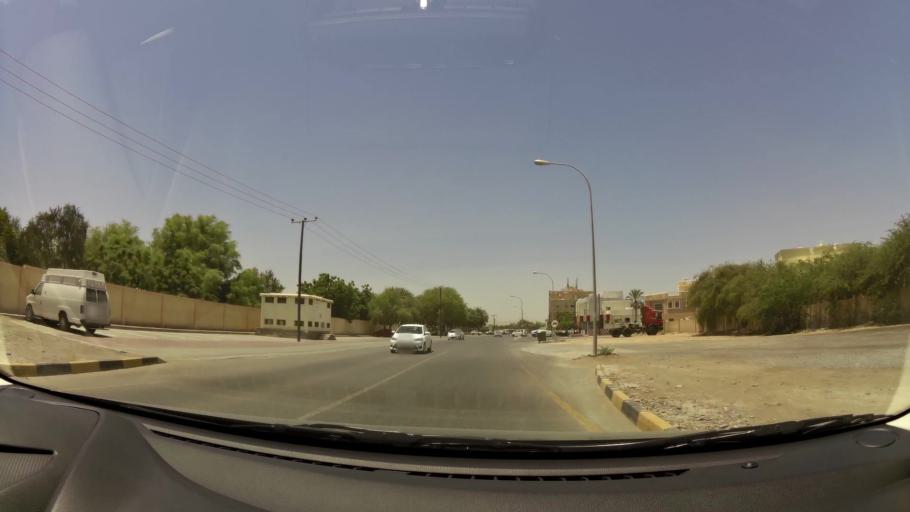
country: OM
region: Muhafazat Masqat
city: As Sib al Jadidah
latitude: 23.6297
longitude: 58.2482
